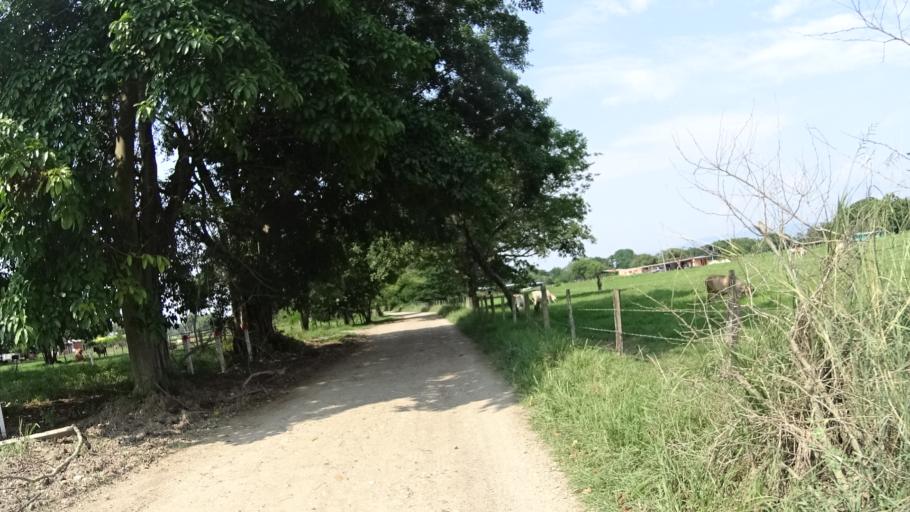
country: CO
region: Cundinamarca
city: Puerto Salgar
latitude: 5.5244
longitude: -74.6870
